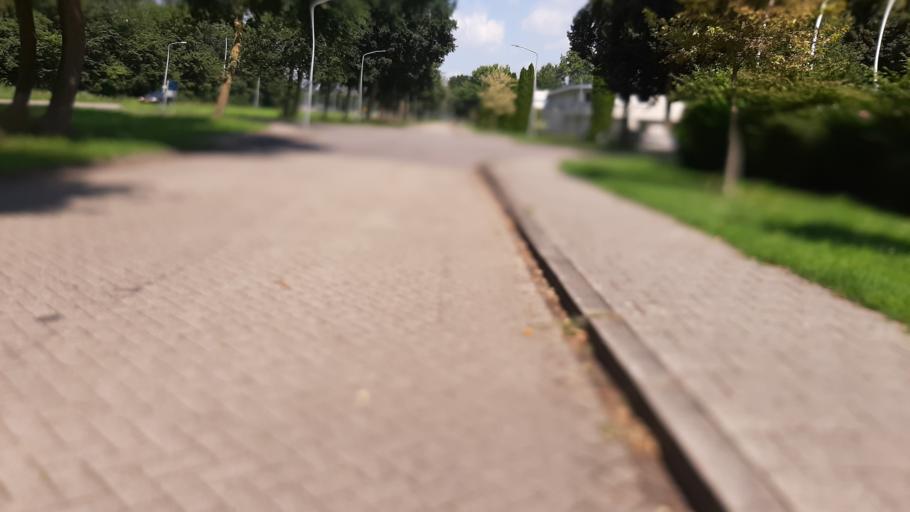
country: NL
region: Flevoland
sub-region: Gemeente Zeewolde
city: Zeewolde
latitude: 52.3240
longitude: 5.5306
